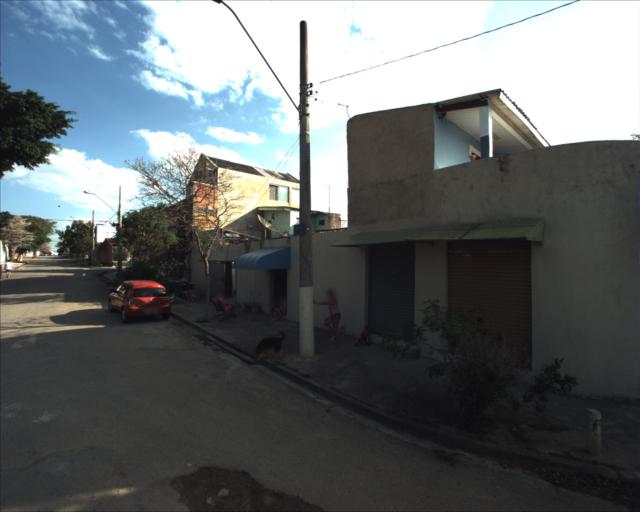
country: BR
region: Sao Paulo
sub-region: Sorocaba
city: Sorocaba
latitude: -23.4982
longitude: -47.5151
